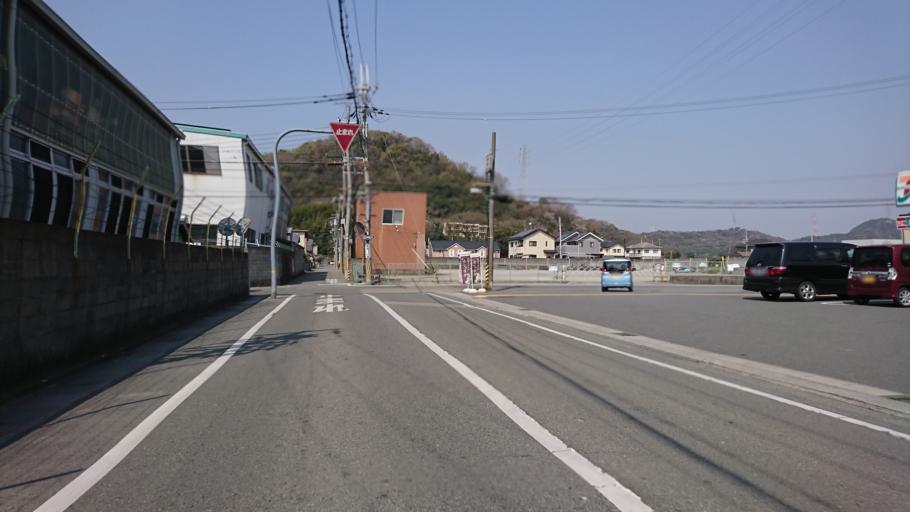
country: JP
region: Hyogo
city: Shirahamacho-usazakiminami
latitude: 34.7886
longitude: 134.7513
